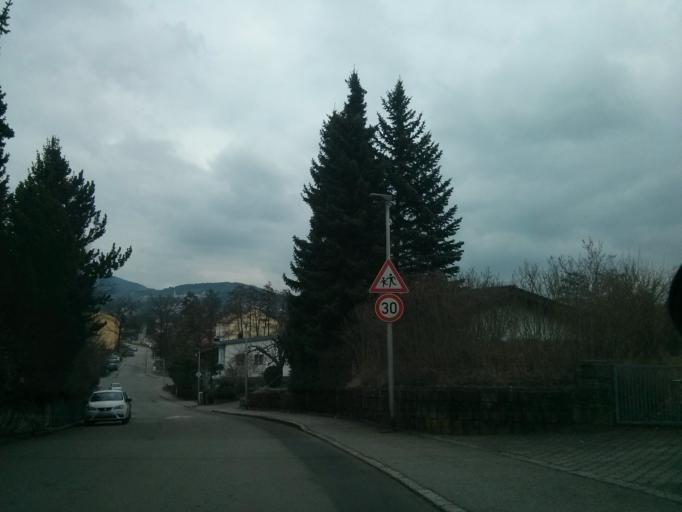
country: DE
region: Bavaria
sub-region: Lower Bavaria
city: Deggendorf
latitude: 48.8388
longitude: 12.9427
